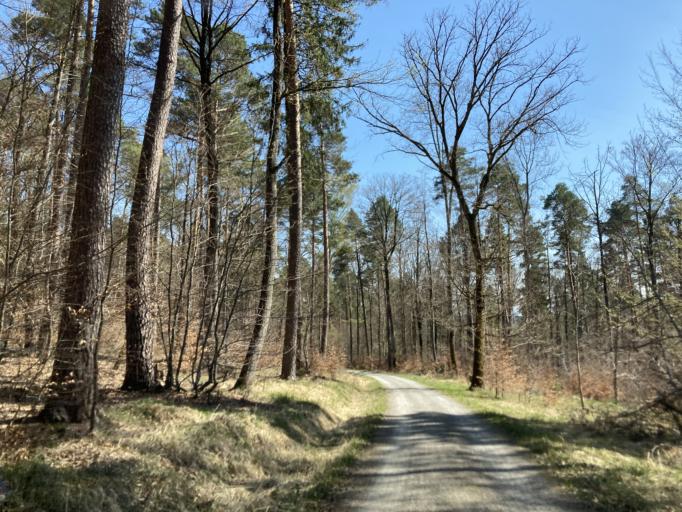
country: DE
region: Baden-Wuerttemberg
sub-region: Tuebingen Region
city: Tuebingen
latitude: 48.5704
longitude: 9.0160
